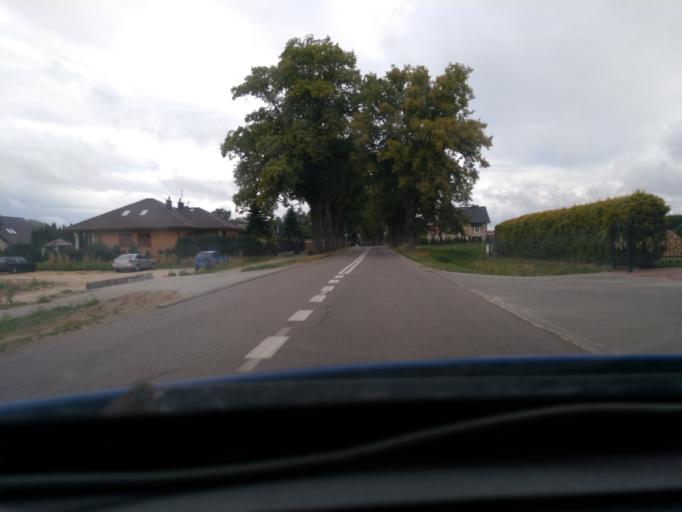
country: PL
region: Pomeranian Voivodeship
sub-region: Powiat kartuski
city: Banino
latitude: 54.3743
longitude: 18.3800
